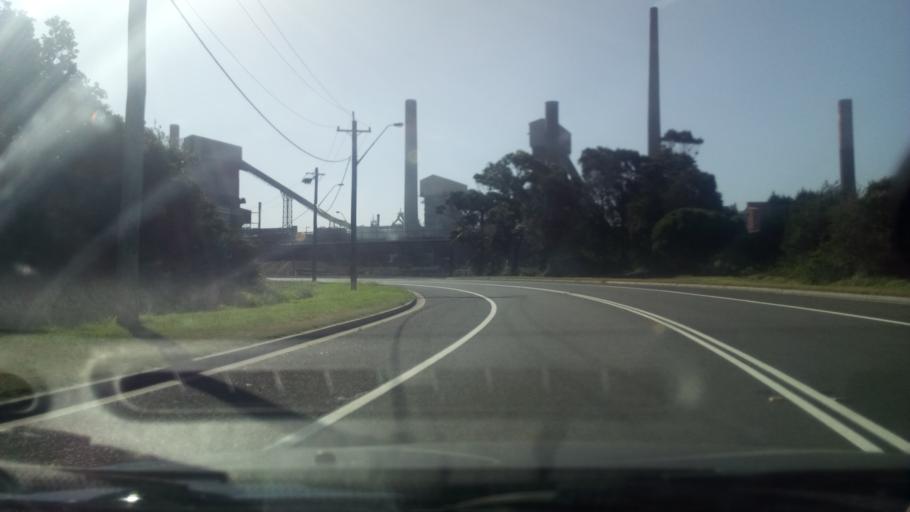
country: AU
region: New South Wales
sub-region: Wollongong
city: Port Kembla
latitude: -34.4692
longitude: 150.8975
